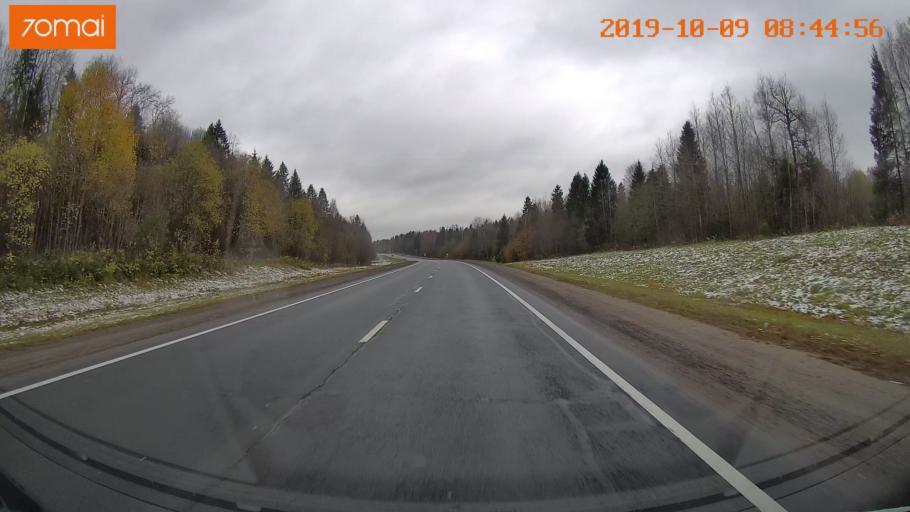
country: RU
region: Vologda
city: Gryazovets
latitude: 59.0428
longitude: 40.1014
